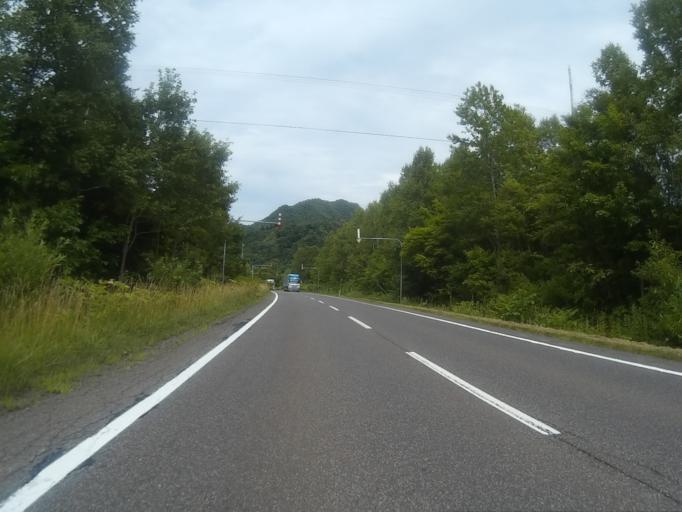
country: JP
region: Hokkaido
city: Sapporo
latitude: 42.9485
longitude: 141.1450
